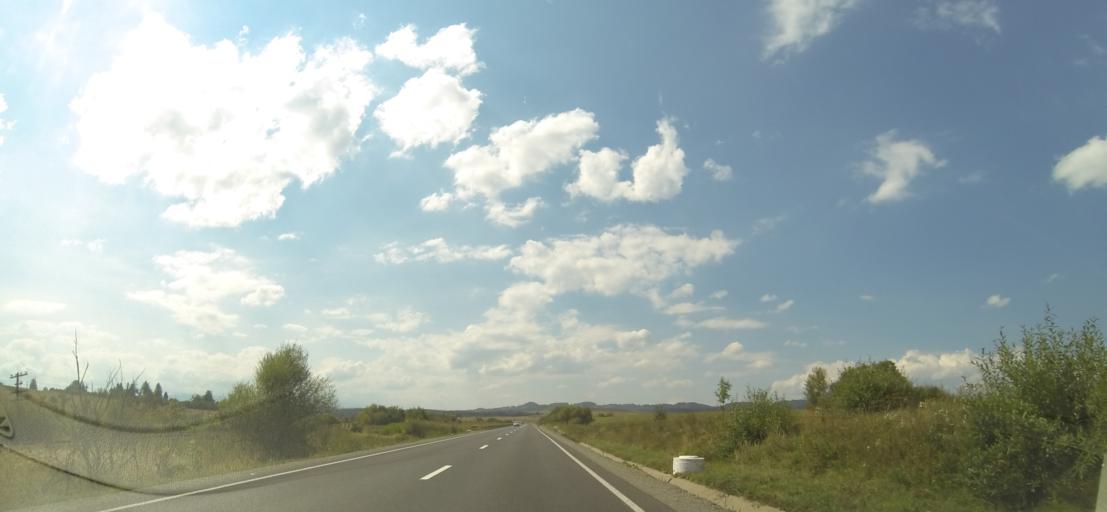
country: RO
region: Brasov
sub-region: Comuna Dumbravita
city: Dumbravita
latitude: 45.7729
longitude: 25.3448
